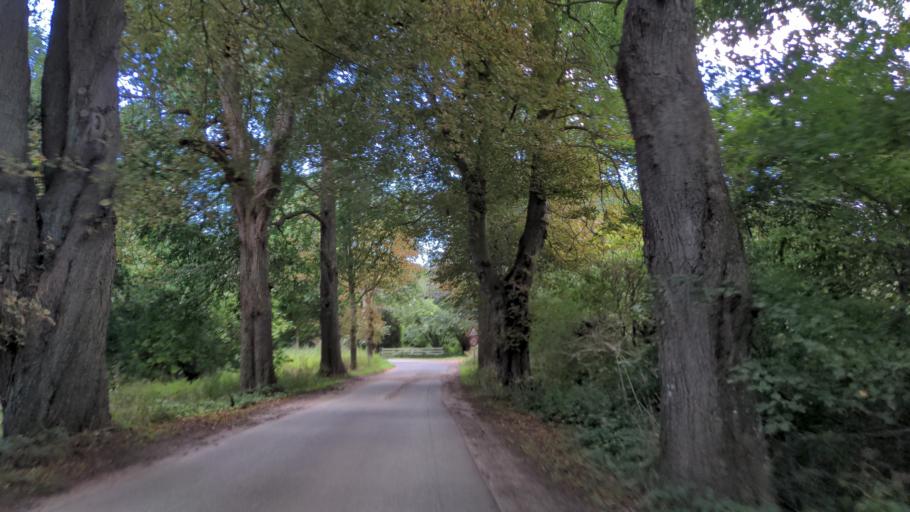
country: DE
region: Schleswig-Holstein
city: Kasseedorf
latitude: 54.1606
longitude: 10.6890
